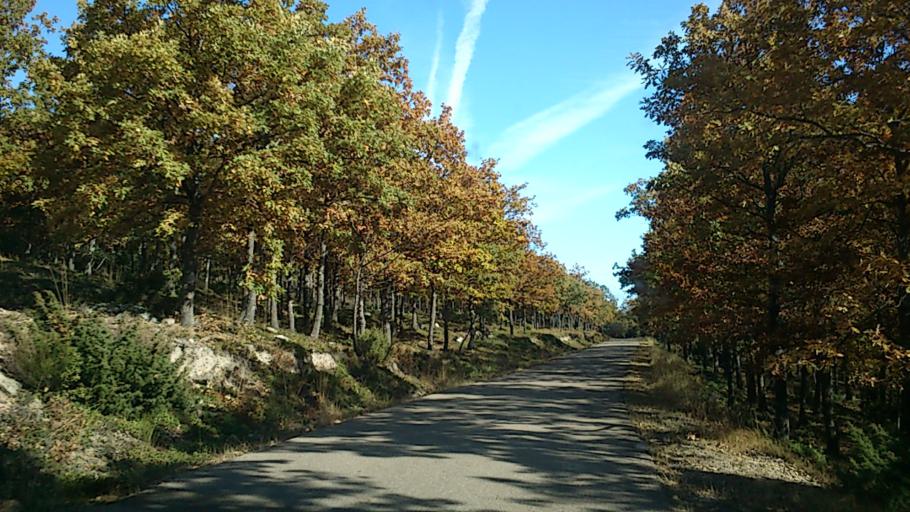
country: ES
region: Aragon
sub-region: Provincia de Zaragoza
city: Litago
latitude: 41.8005
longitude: -1.7888
